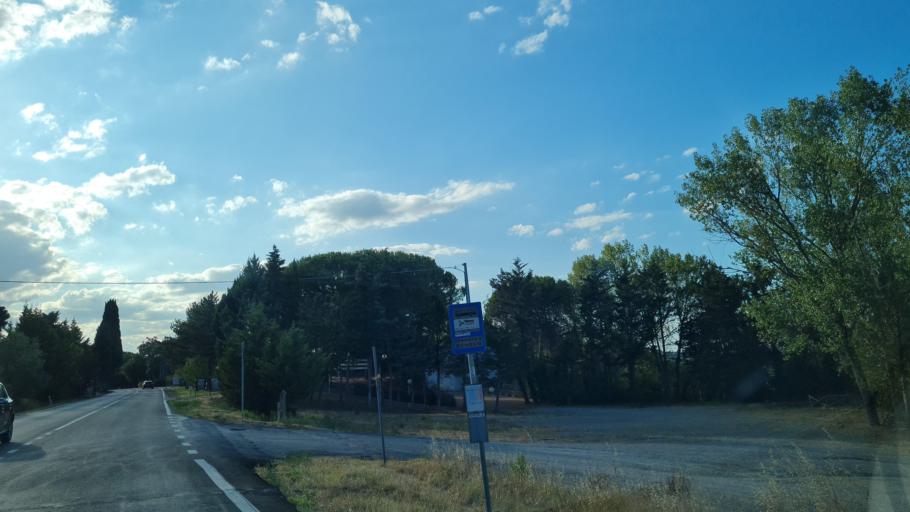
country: IT
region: Tuscany
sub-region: Provincia di Siena
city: Sarteano
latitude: 43.0277
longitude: 11.8706
